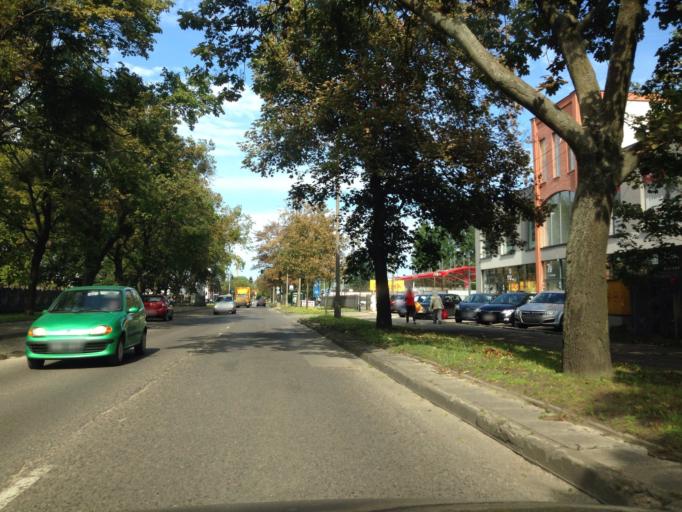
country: PL
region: Pomeranian Voivodeship
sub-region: Gdansk
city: Gdansk
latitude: 54.3934
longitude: 18.6173
